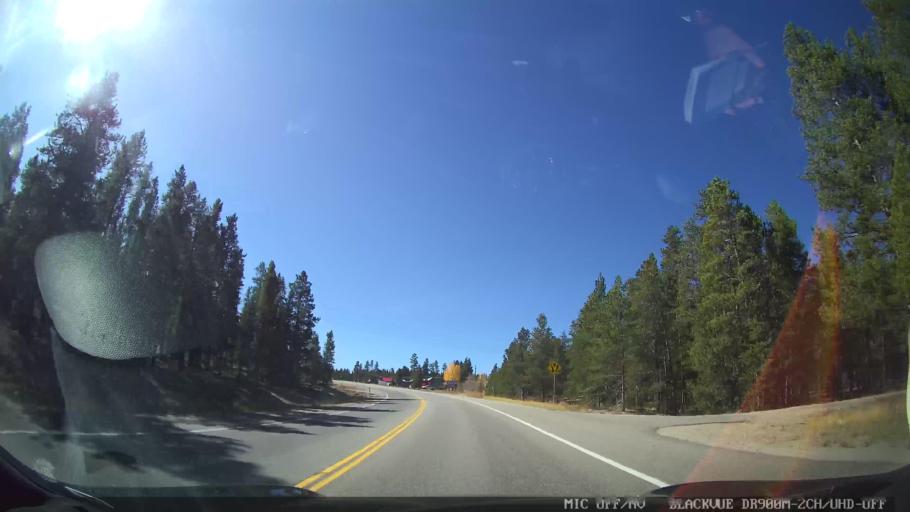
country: US
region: Colorado
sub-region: Lake County
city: Leadville North
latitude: 39.2697
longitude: -106.2899
